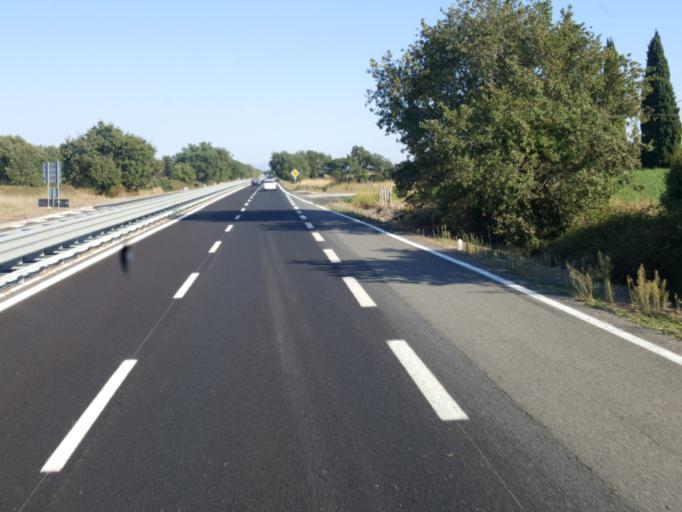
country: IT
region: Latium
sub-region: Provincia di Viterbo
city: Tarquinia
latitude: 42.2920
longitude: 11.6815
